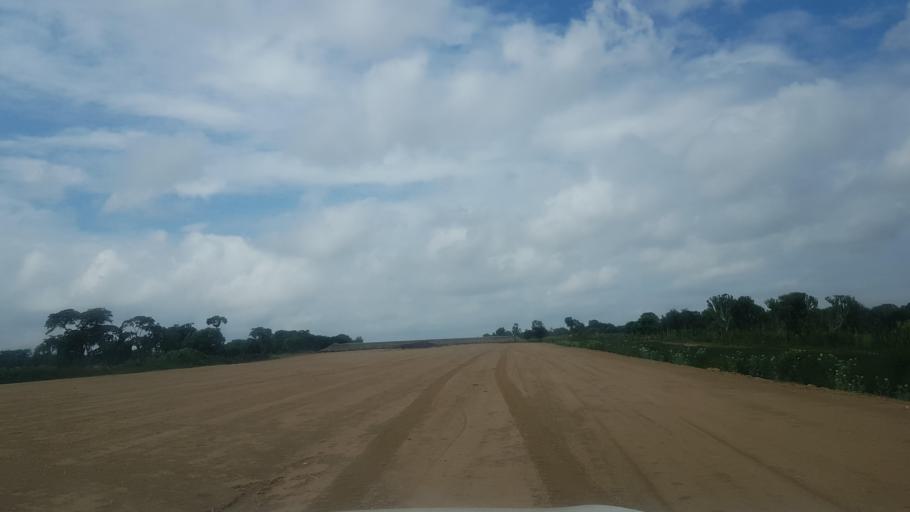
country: ET
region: Oromiya
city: Shashemene
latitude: 7.2684
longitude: 38.5981
